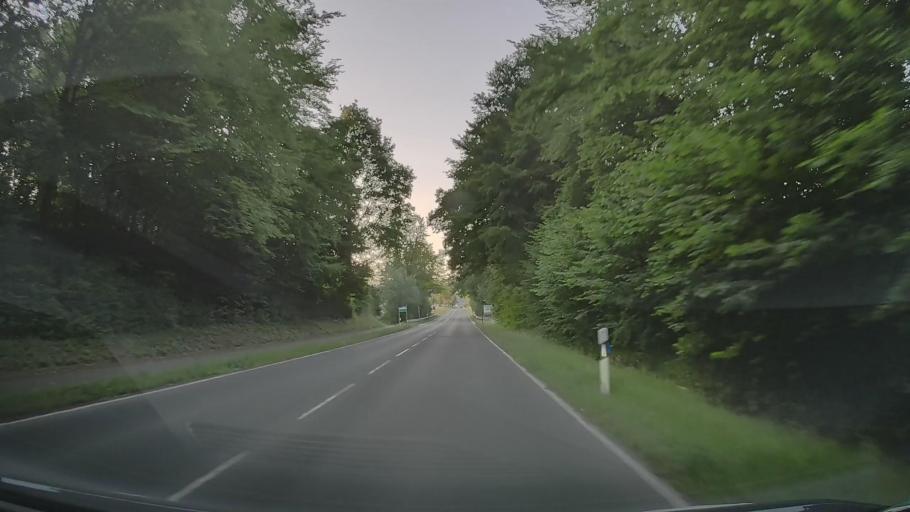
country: DE
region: North Rhine-Westphalia
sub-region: Regierungsbezirk Detmold
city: Lugde
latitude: 51.9741
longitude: 9.2322
